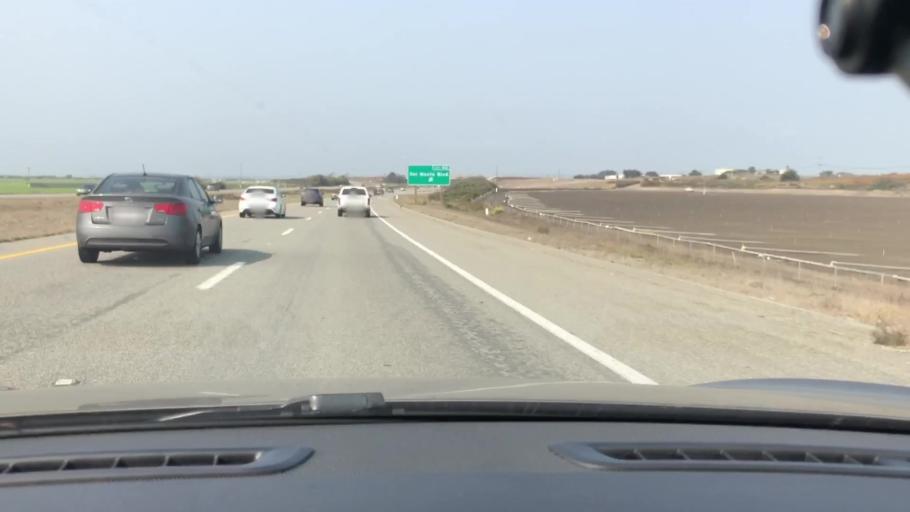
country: US
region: California
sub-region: Monterey County
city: Marina
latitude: 36.7163
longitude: -121.7933
